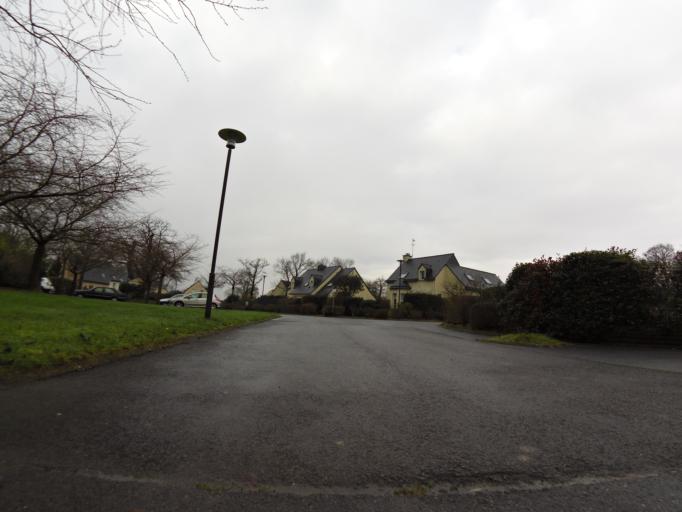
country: FR
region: Brittany
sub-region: Departement d'Ille-et-Vilaine
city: Laille
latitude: 47.9760
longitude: -1.7221
